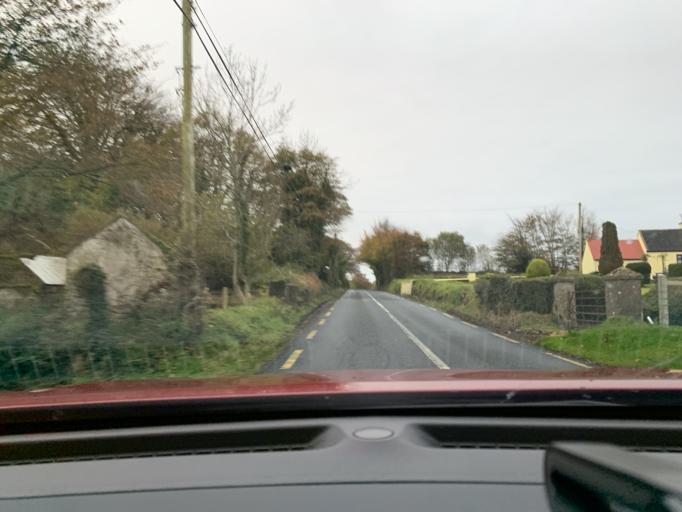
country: IE
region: Connaught
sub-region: Roscommon
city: Ballaghaderreen
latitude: 53.9775
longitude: -8.5356
